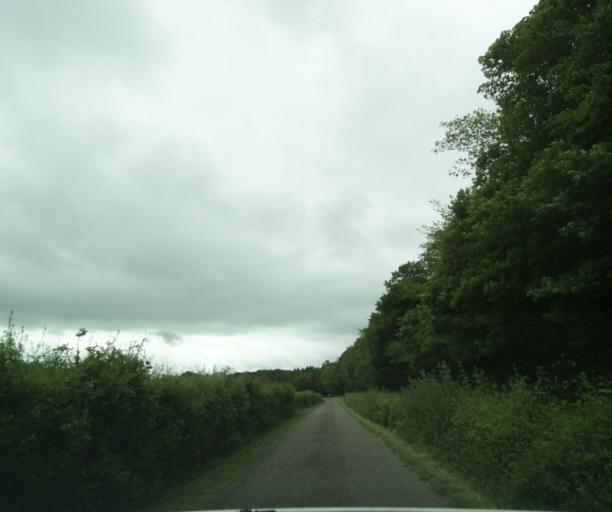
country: FR
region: Bourgogne
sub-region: Departement de Saone-et-Loire
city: Charolles
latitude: 46.4486
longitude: 4.2693
